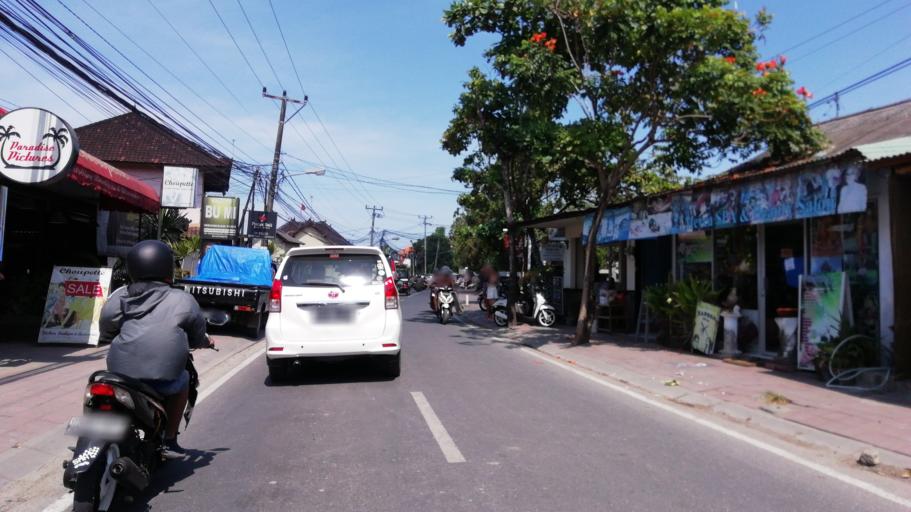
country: ID
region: Bali
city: Banjar Kerobokan
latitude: -8.6510
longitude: 115.1355
